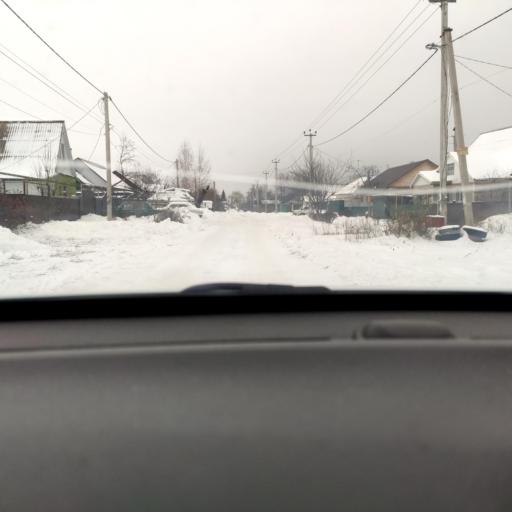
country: RU
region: Voronezj
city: Volya
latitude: 51.7528
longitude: 39.5001
